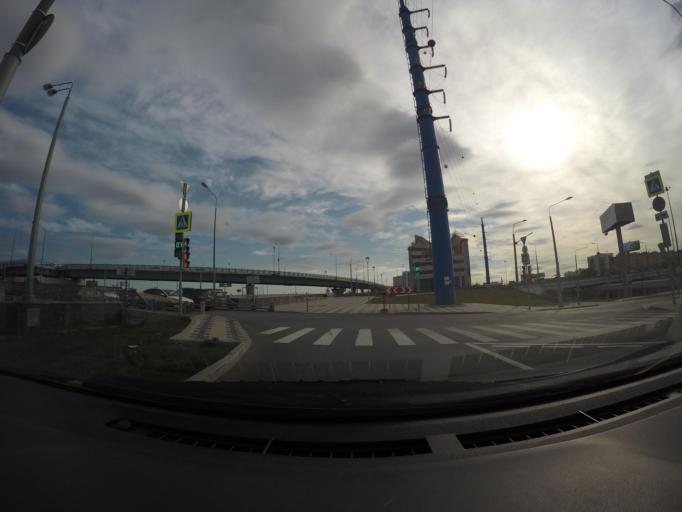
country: RU
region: Moskovskaya
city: Bogorodskoye
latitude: 55.8027
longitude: 37.7481
